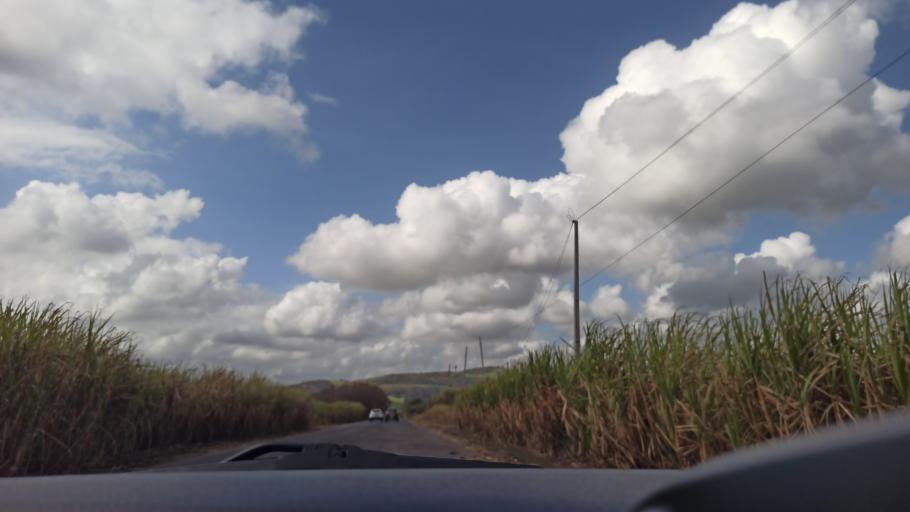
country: BR
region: Paraiba
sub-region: Juripiranga
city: Juripiranga
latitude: -7.4056
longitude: -35.2593
